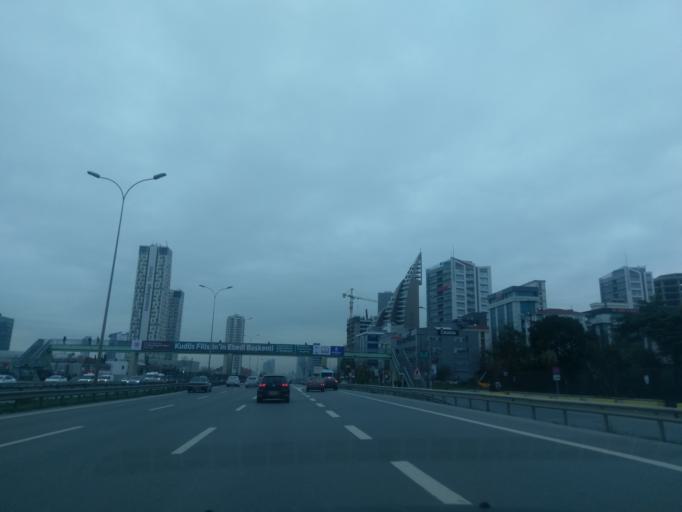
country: TR
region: Istanbul
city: Maltepe
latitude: 40.9086
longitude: 29.2054
